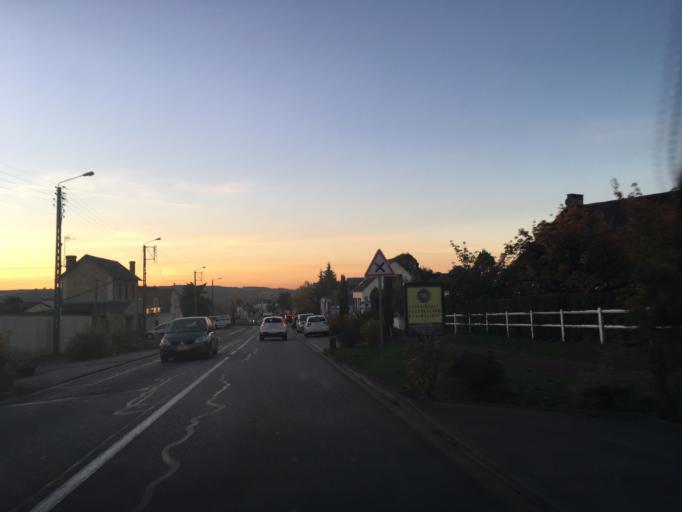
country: FR
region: Haute-Normandie
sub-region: Departement de l'Eure
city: Pacy-sur-Eure
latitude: 49.0126
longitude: 1.3907
